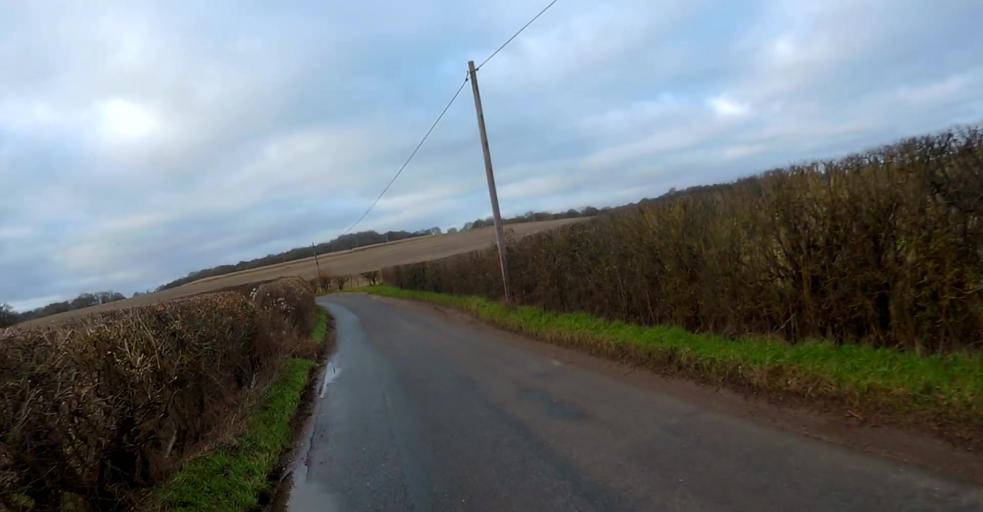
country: GB
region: England
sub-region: Hampshire
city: Basingstoke
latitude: 51.1857
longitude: -1.1376
